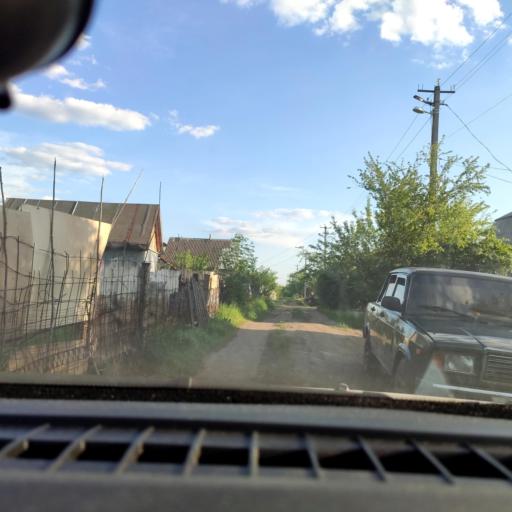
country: RU
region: Voronezj
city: Maslovka
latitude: 51.5195
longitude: 39.2383
